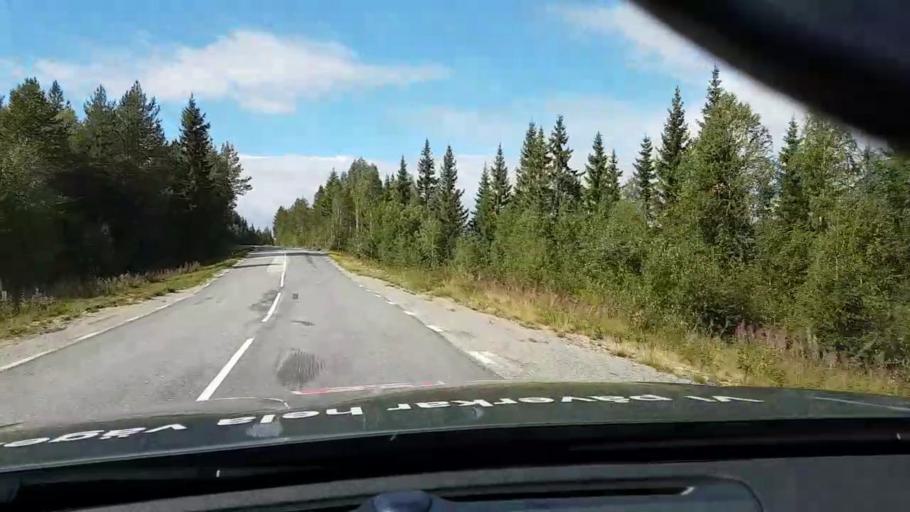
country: SE
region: Vaesterbotten
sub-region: Asele Kommun
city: Asele
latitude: 63.8148
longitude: 17.5033
